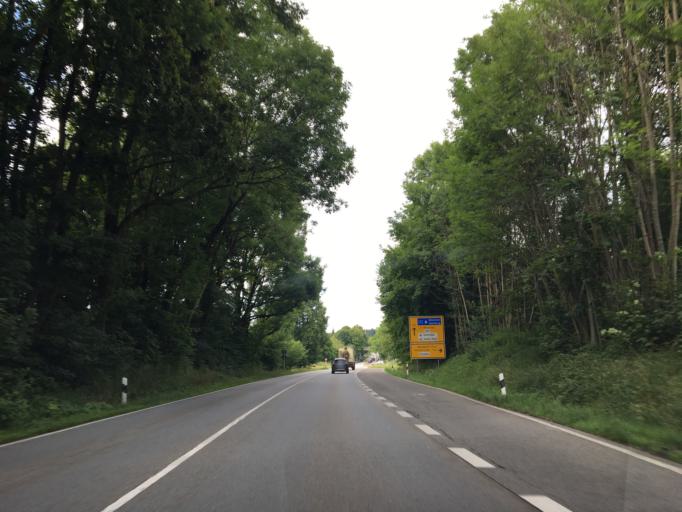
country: DE
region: Bavaria
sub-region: Upper Bavaria
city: Holzkirchen
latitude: 47.8739
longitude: 11.7179
